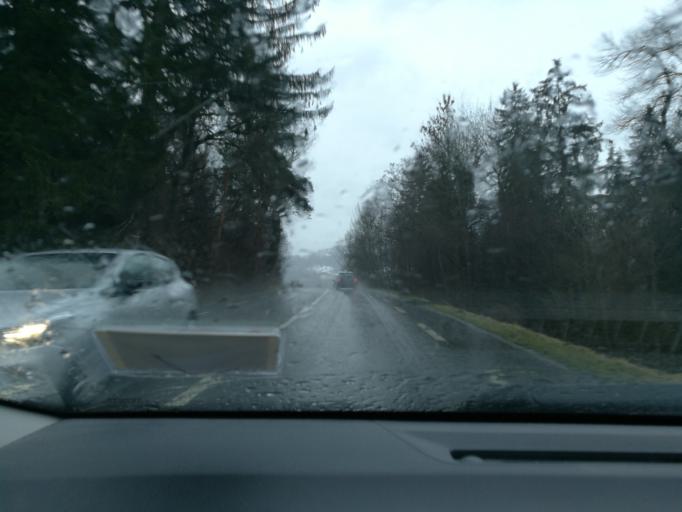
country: FR
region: Rhone-Alpes
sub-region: Departement de la Haute-Savoie
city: Domancy
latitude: 45.9277
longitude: 6.6561
